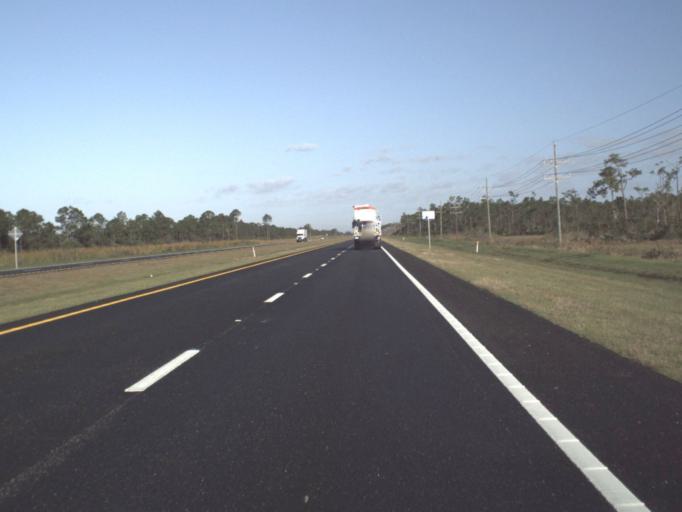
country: US
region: Florida
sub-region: Martin County
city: Indiantown
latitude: 26.9272
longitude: -80.3278
